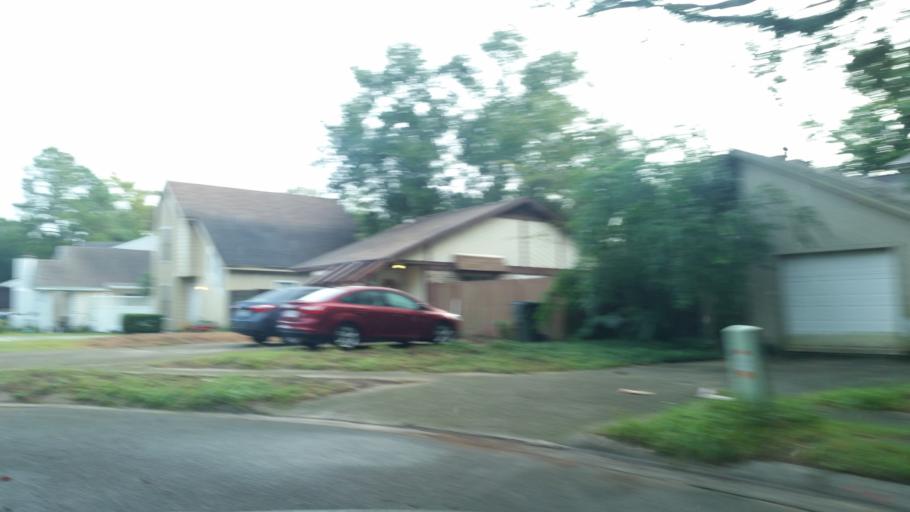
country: US
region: Florida
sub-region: Escambia County
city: Ferry Pass
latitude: 30.5064
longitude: -87.1980
